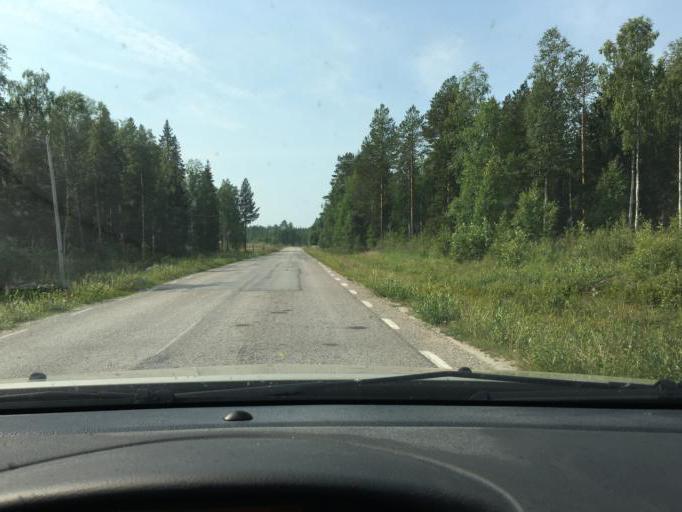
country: SE
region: Norrbotten
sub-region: Kalix Kommun
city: Rolfs
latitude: 65.7722
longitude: 22.9804
